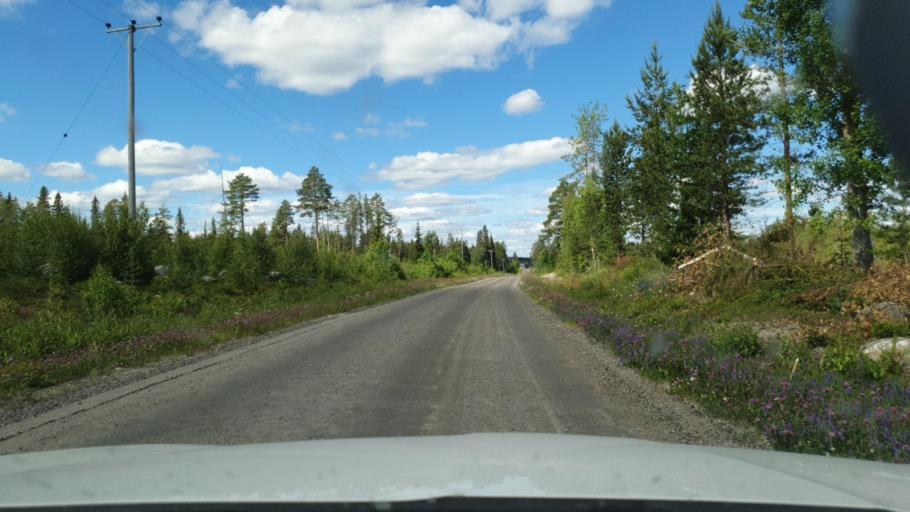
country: SE
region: Vaesterbotten
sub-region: Skelleftea Kommun
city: Backa
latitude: 65.1777
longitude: 21.0823
